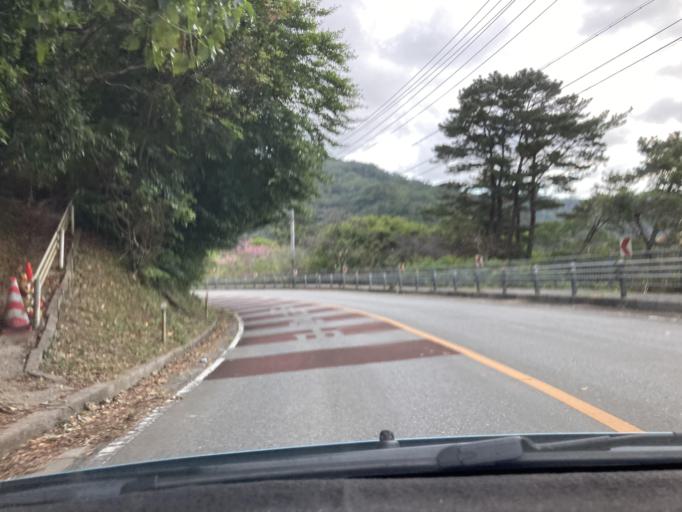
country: JP
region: Okinawa
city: Nago
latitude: 26.8313
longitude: 128.2831
